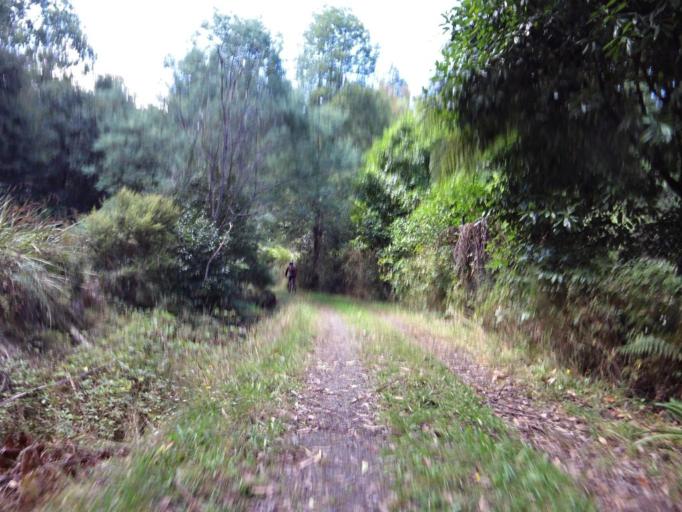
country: AU
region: Victoria
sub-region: Yarra Ranges
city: Millgrove
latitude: -37.7023
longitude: 145.7847
